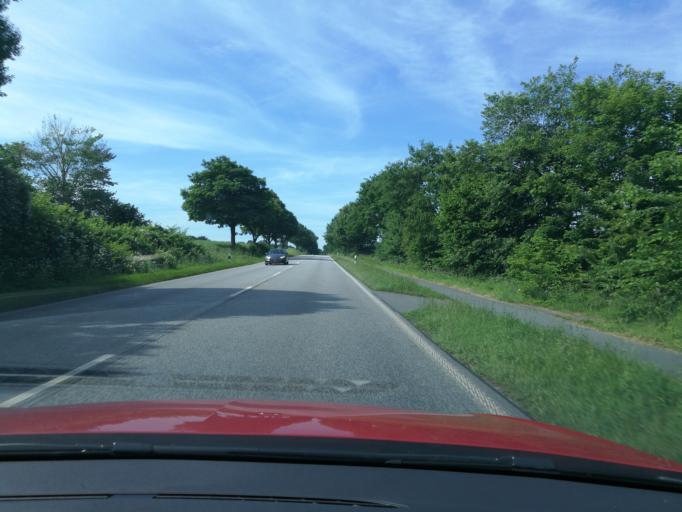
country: DE
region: Schleswig-Holstein
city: Neritz
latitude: 53.7808
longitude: 10.2789
